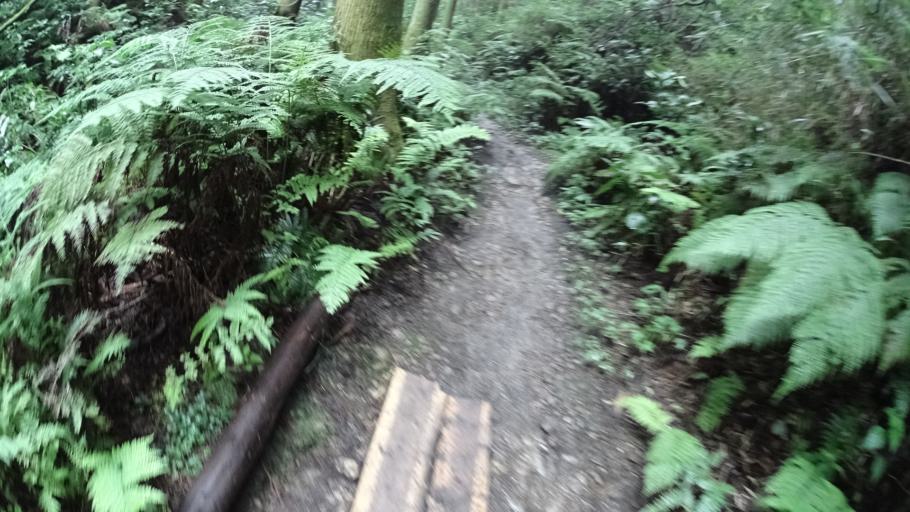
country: JP
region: Kanagawa
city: Yokosuka
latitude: 35.2554
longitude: 139.6340
